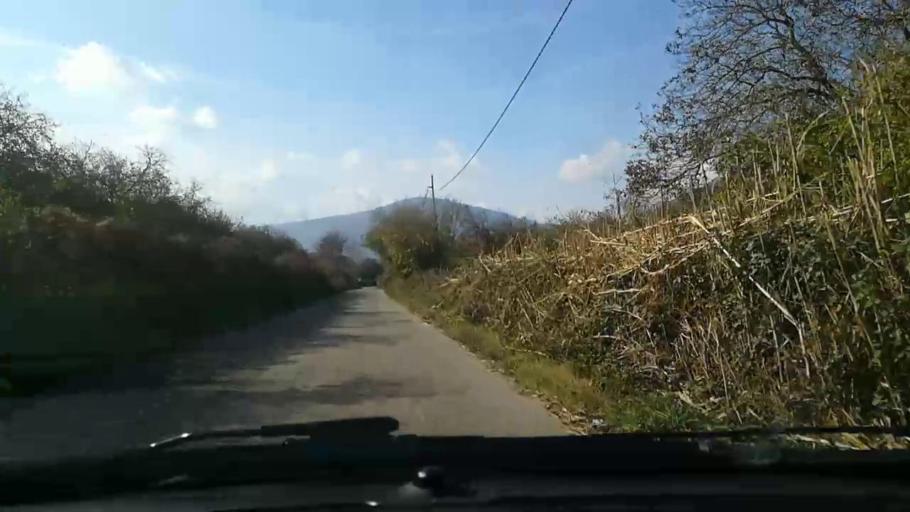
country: IT
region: Latium
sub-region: Provincia di Viterbo
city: Caprarola
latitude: 42.3351
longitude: 12.2020
